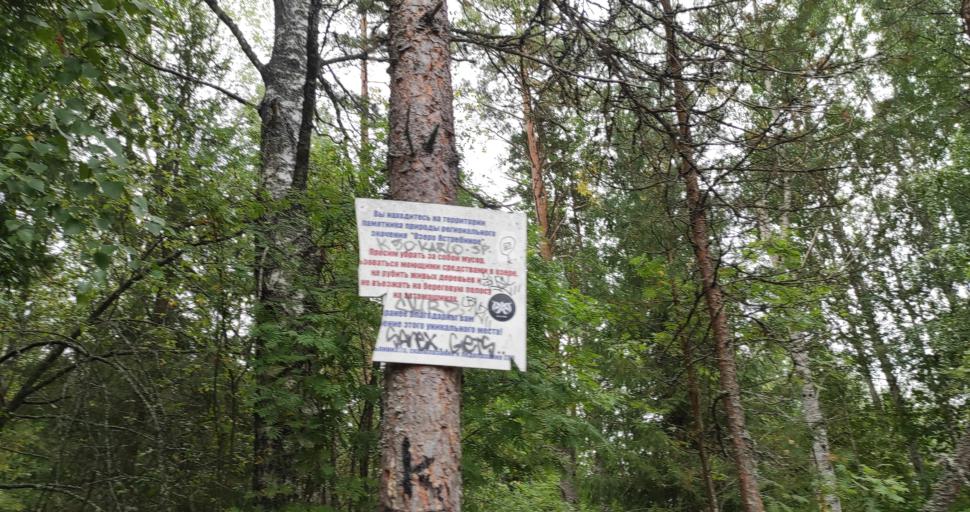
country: RU
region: Leningrad
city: Kuznechnoye
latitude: 61.1746
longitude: 29.6942
